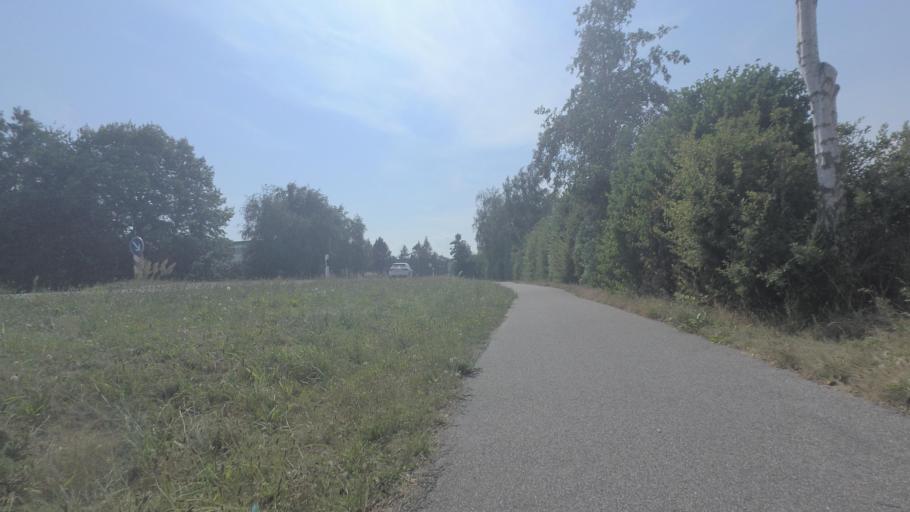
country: DE
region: Mecklenburg-Vorpommern
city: Poseritz
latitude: 54.2168
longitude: 13.2552
